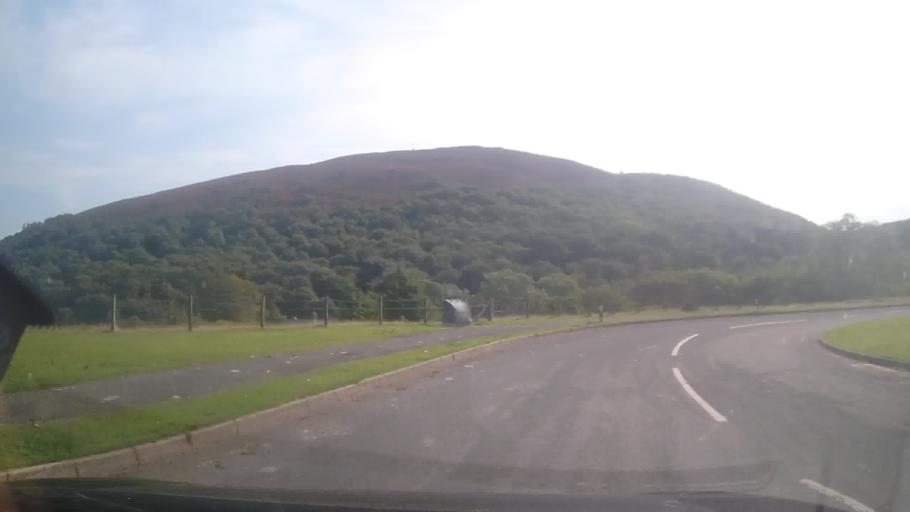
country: GB
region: Wales
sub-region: Sir Powys
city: Rhayader
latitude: 52.2750
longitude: -3.5671
